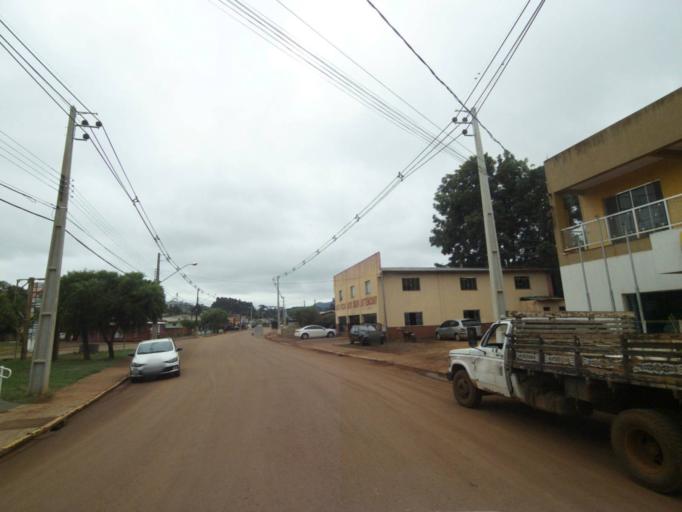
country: BR
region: Parana
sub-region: Pitanga
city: Pitanga
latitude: -24.9350
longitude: -51.8715
